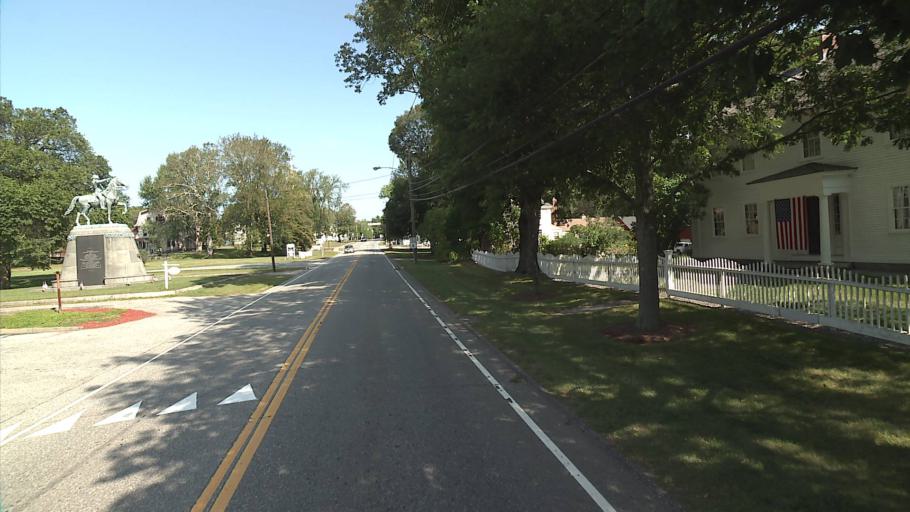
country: US
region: Connecticut
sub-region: Windham County
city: East Brooklyn
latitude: 41.7861
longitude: -71.9496
